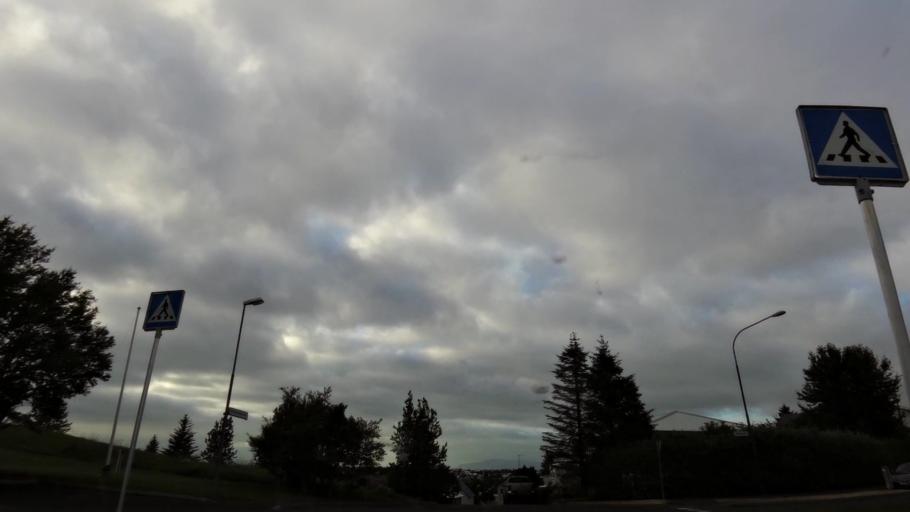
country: IS
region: Capital Region
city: Hafnarfjoerdur
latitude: 64.0610
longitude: -21.9541
